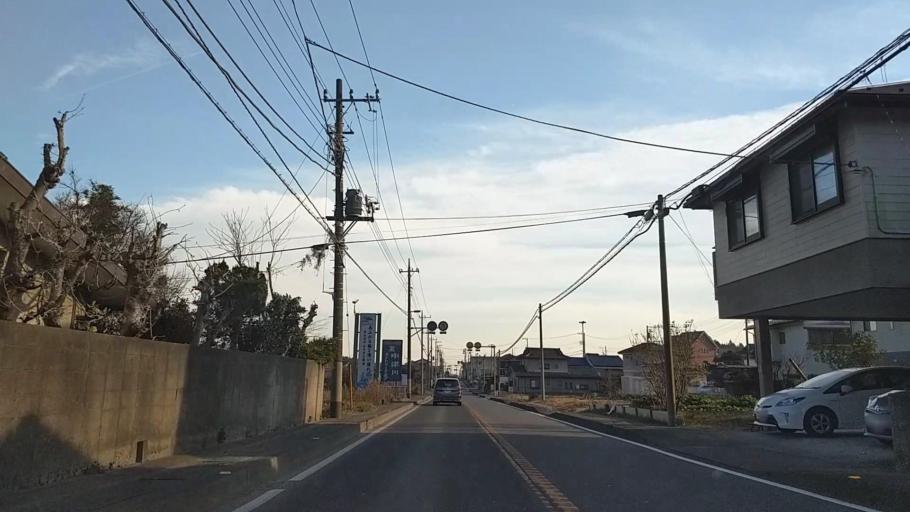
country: JP
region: Kanagawa
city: Zama
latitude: 35.5152
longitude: 139.2978
